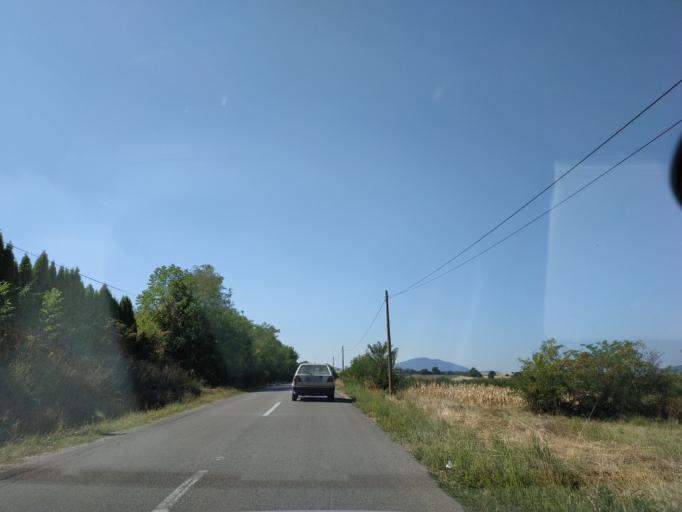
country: RS
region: Central Serbia
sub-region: Sumadijski Okrug
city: Topola
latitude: 44.2714
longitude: 20.6475
